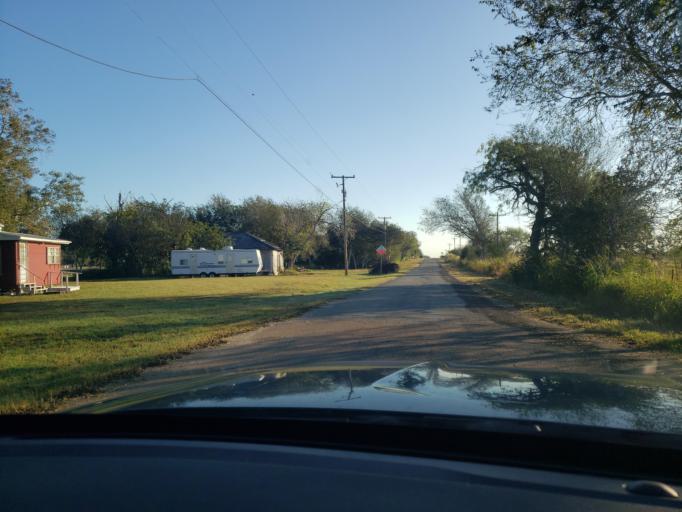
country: US
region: Texas
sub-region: Bee County
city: Beeville
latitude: 28.4164
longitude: -97.7212
